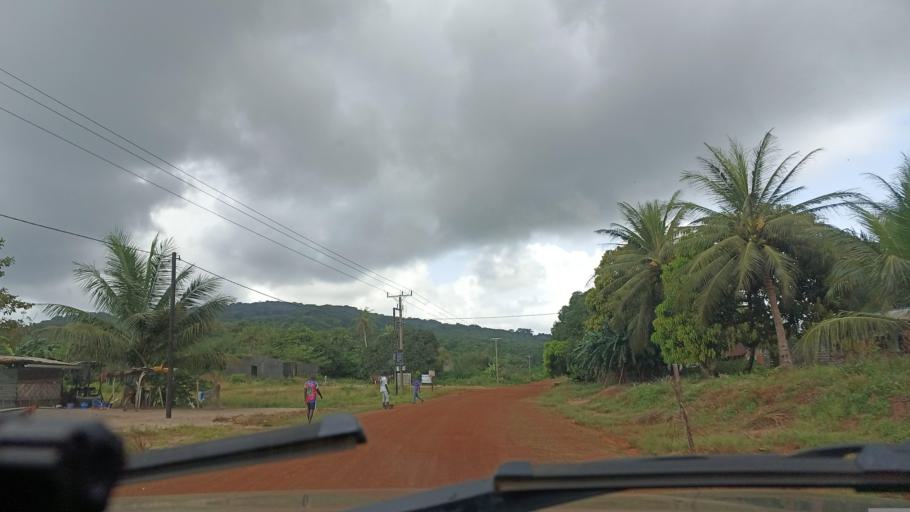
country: LR
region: Grand Cape Mount
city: Robertsport
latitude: 6.7064
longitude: -11.3336
